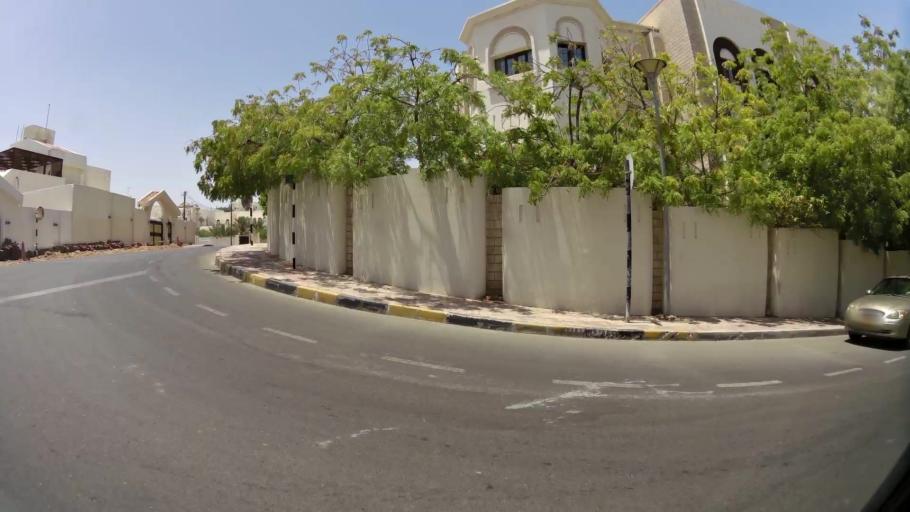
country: OM
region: Muhafazat Masqat
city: Bawshar
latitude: 23.6094
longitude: 58.4708
